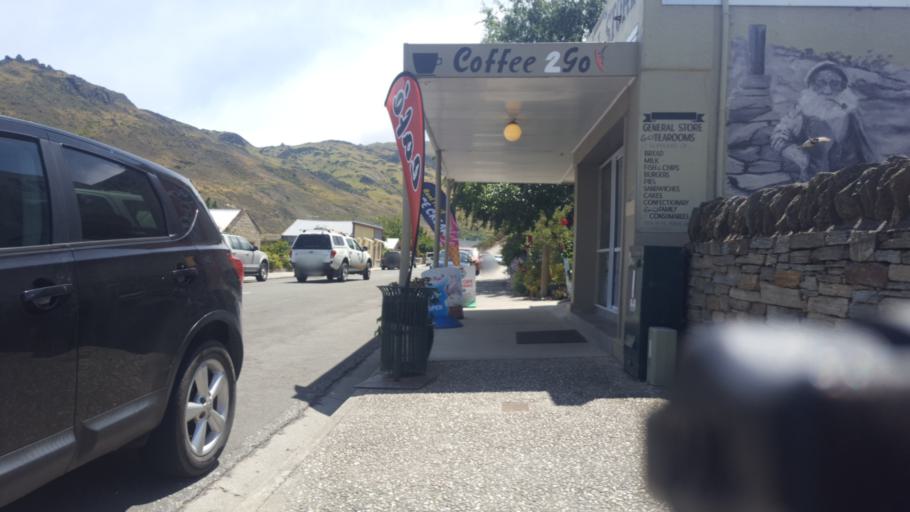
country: NZ
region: Otago
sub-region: Queenstown-Lakes District
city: Wanaka
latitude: -45.1862
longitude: 169.3155
